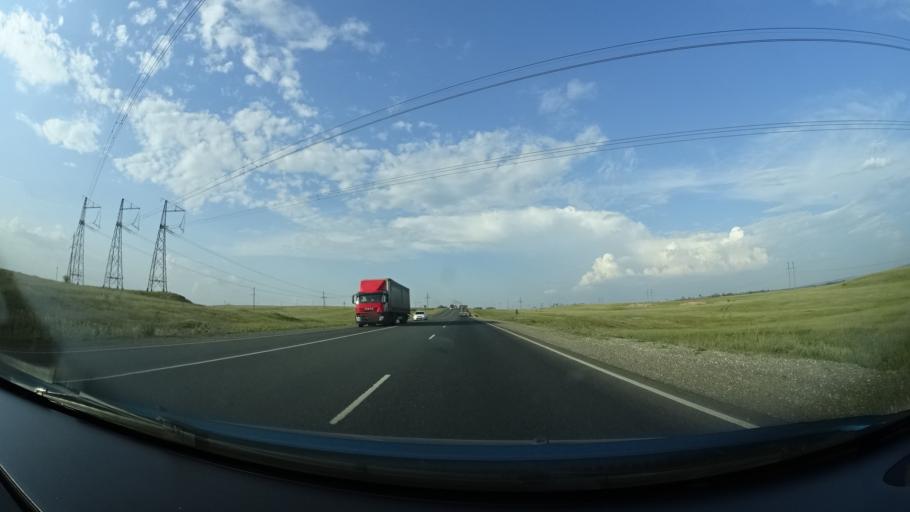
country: RU
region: Samara
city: Sukhodol
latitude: 53.7017
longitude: 50.8062
